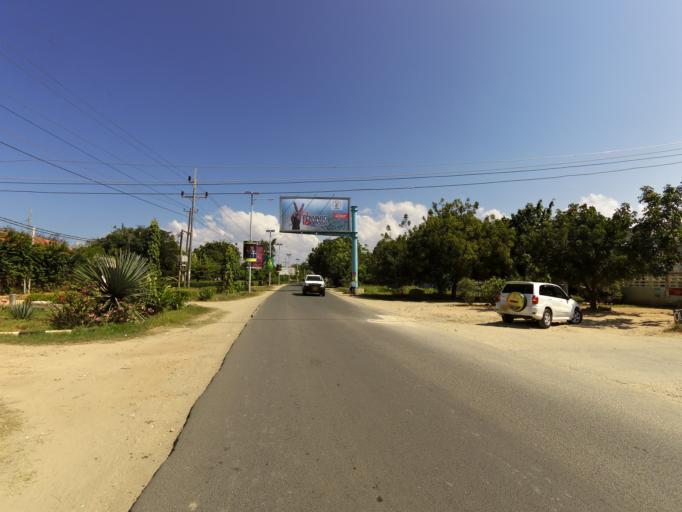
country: TZ
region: Dar es Salaam
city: Magomeni
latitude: -6.7501
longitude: 39.2844
